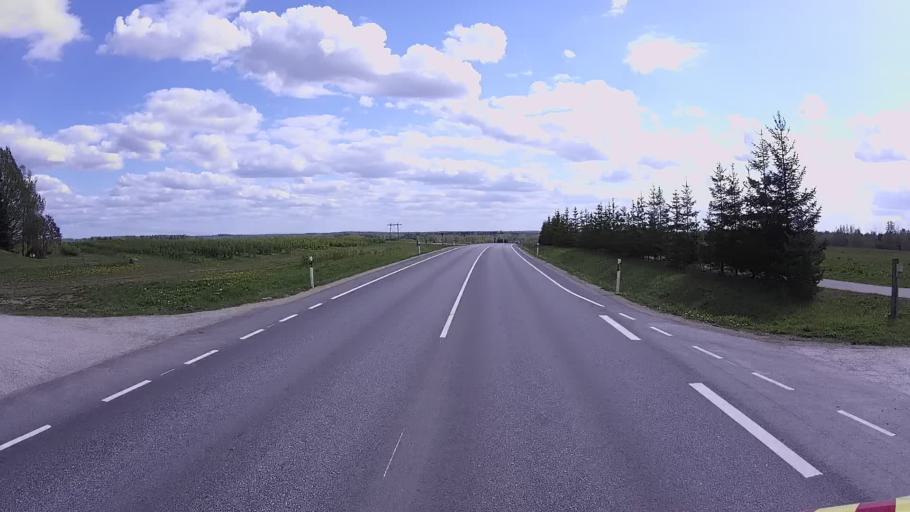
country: EE
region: Tartu
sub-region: Tartu linn
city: Tartu
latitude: 58.4775
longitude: 26.6828
